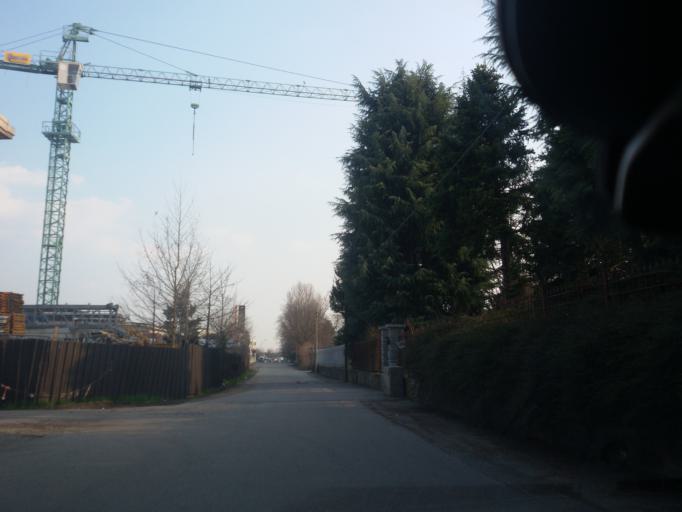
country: IT
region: Piedmont
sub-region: Provincia di Torino
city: Savonera
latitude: 45.1023
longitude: 7.6110
